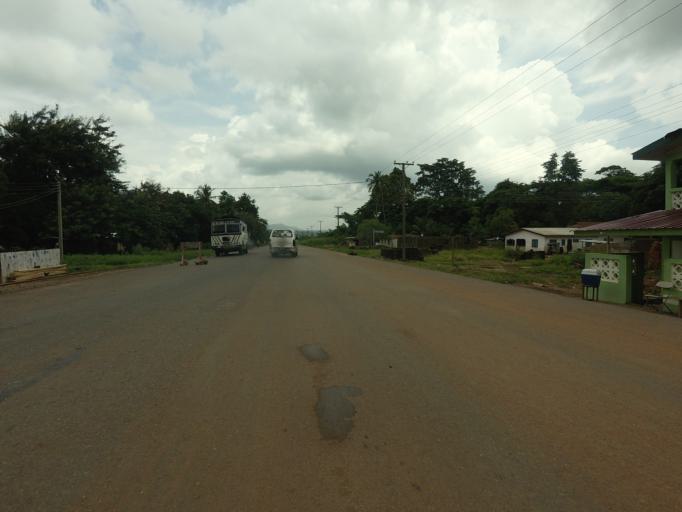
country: GH
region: Volta
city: Ho
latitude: 6.6228
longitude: 0.3086
